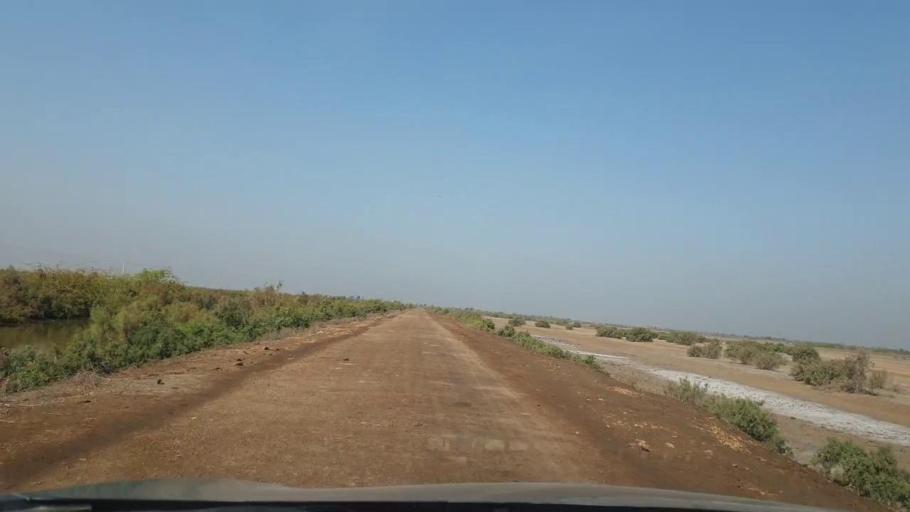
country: PK
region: Sindh
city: Berani
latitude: 25.6960
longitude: 68.8740
